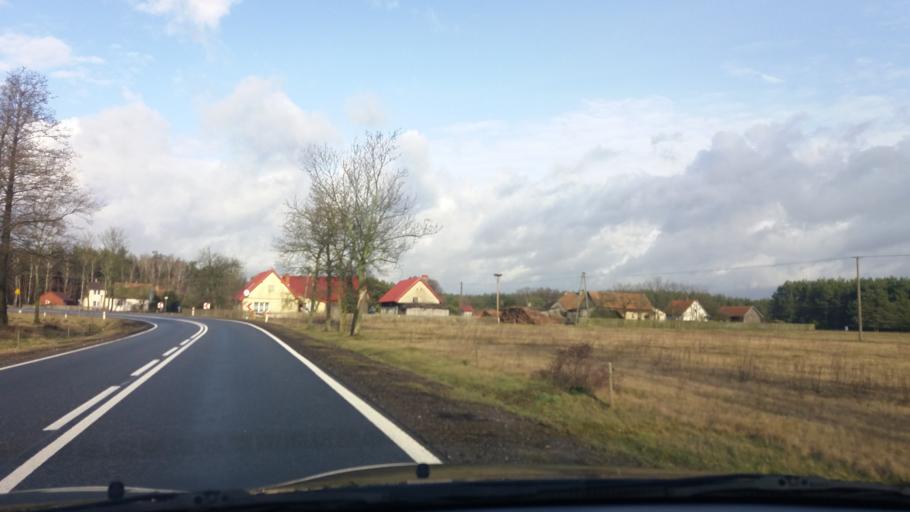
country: PL
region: Masovian Voivodeship
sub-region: Powiat przasnyski
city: Chorzele
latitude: 53.2913
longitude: 20.9154
